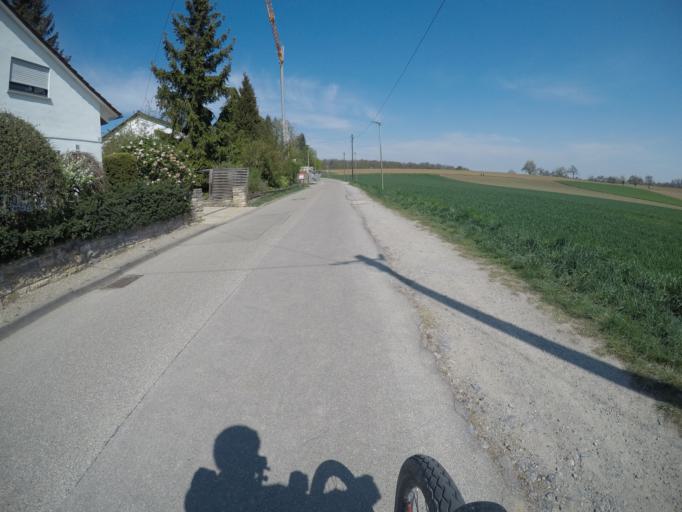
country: DE
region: Baden-Wuerttemberg
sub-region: Regierungsbezirk Stuttgart
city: Rutesheim
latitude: 48.8170
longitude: 8.9769
